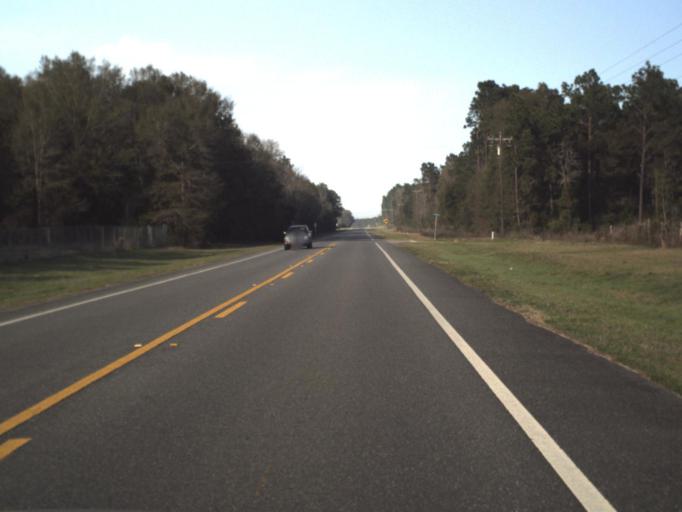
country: US
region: Florida
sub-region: Calhoun County
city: Blountstown
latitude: 30.5126
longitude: -85.1995
